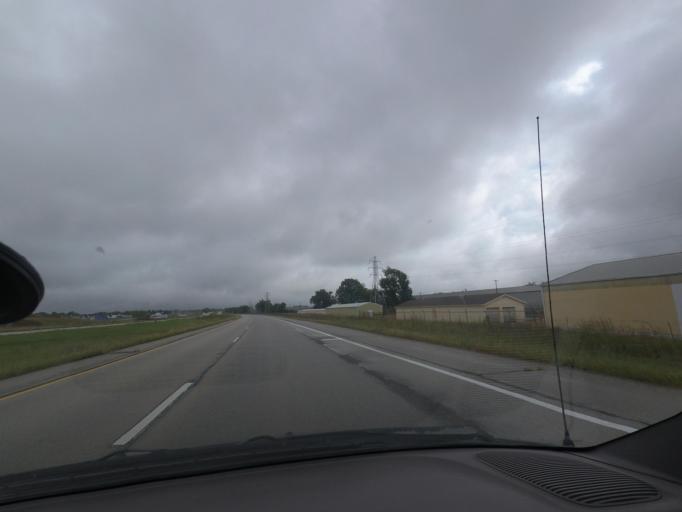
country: US
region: Illinois
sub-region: Piatt County
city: Monticello
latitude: 40.0565
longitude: -88.5587
